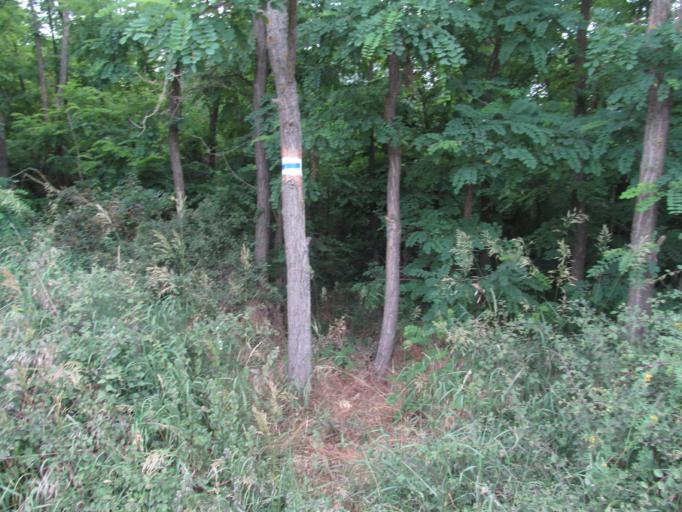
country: HU
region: Veszprem
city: Badacsonytomaj
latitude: 46.8452
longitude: 17.5509
